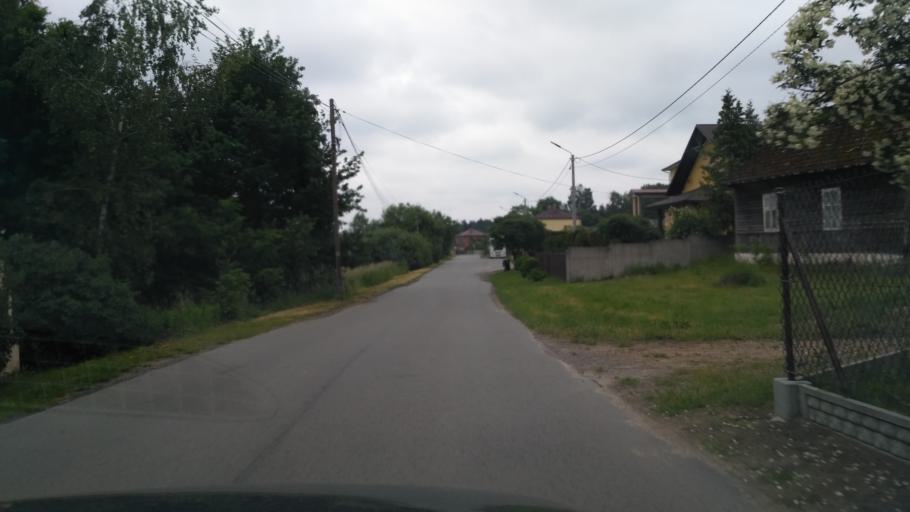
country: PL
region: Subcarpathian Voivodeship
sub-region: Powiat kolbuszowski
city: Niwiska
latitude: 50.2181
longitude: 21.6352
